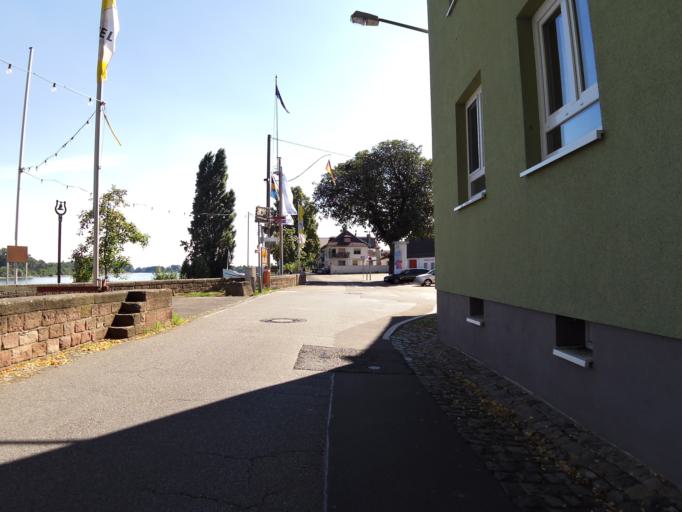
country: DE
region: Rheinland-Pfalz
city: Osthofen
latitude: 49.6978
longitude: 8.3585
